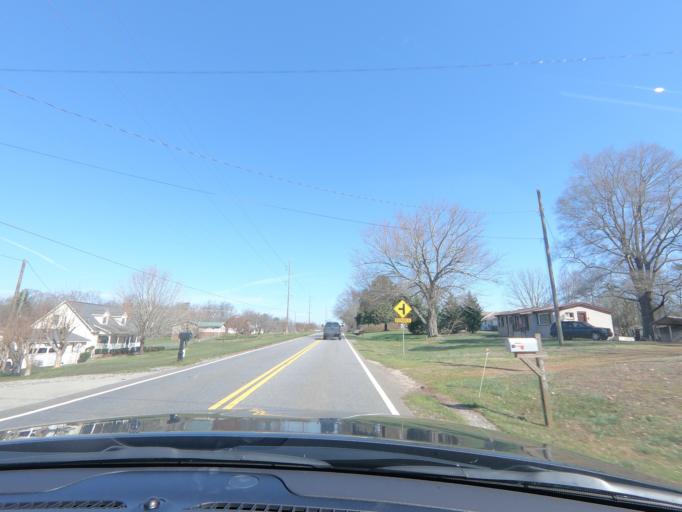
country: US
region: Georgia
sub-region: Forsyth County
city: Cumming
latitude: 34.3153
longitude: -84.1428
